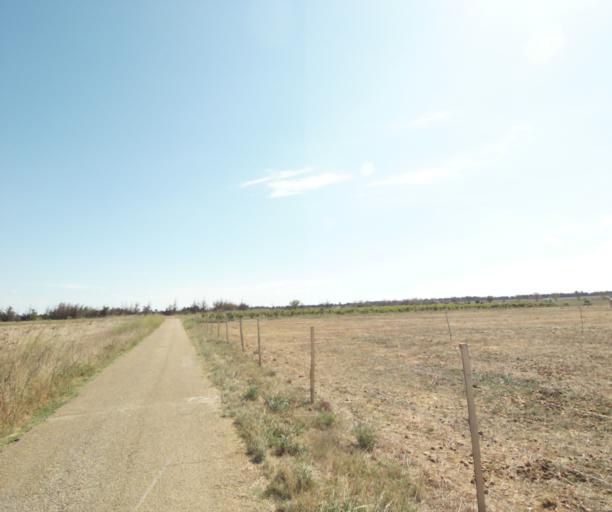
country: FR
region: Languedoc-Roussillon
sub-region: Departement du Gard
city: Bouillargues
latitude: 43.8044
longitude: 4.4504
